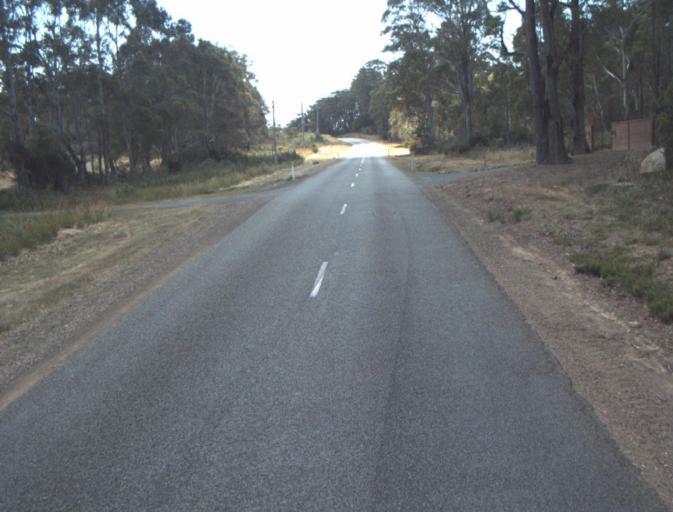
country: AU
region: Tasmania
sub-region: Launceston
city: Mayfield
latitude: -41.3174
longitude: 147.1351
